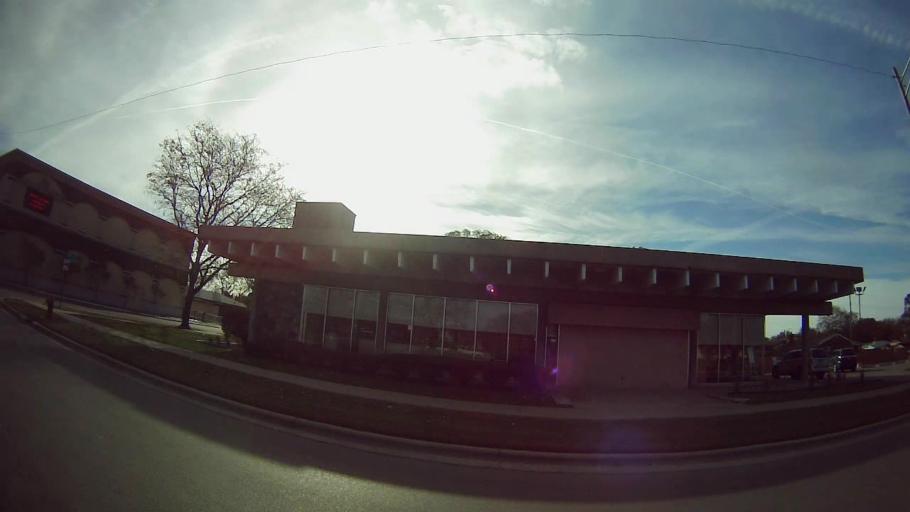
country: US
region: Michigan
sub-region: Oakland County
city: Southfield
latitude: 42.4439
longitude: -83.2337
